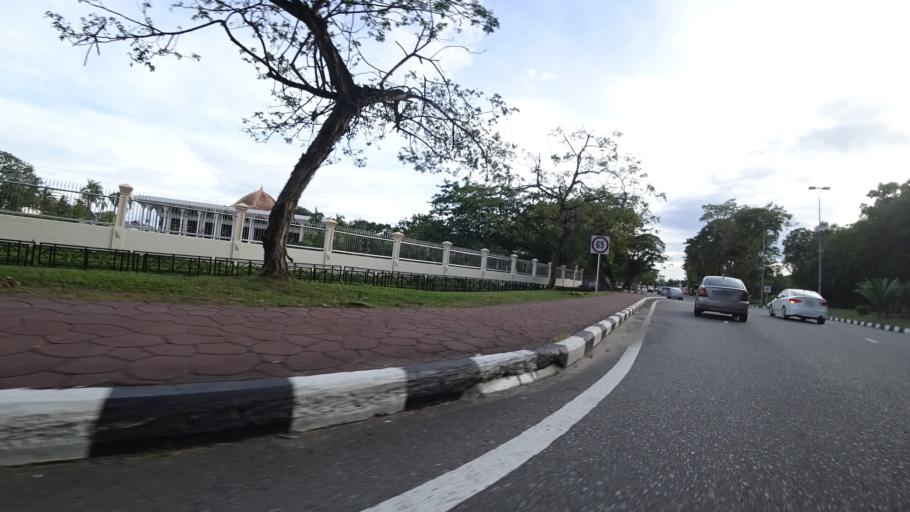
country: BN
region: Brunei and Muara
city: Bandar Seri Begawan
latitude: 4.8922
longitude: 114.9340
